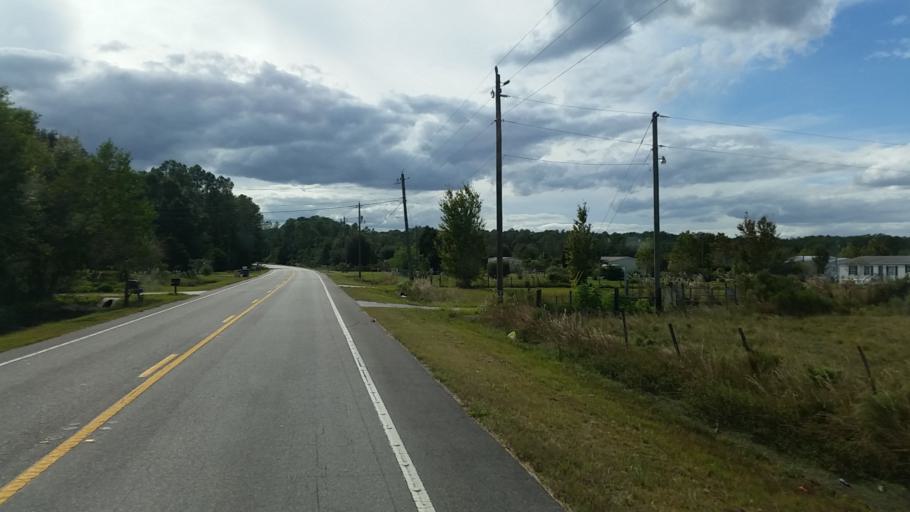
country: US
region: Florida
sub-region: Polk County
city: Gibsonia
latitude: 28.2542
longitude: -81.9631
